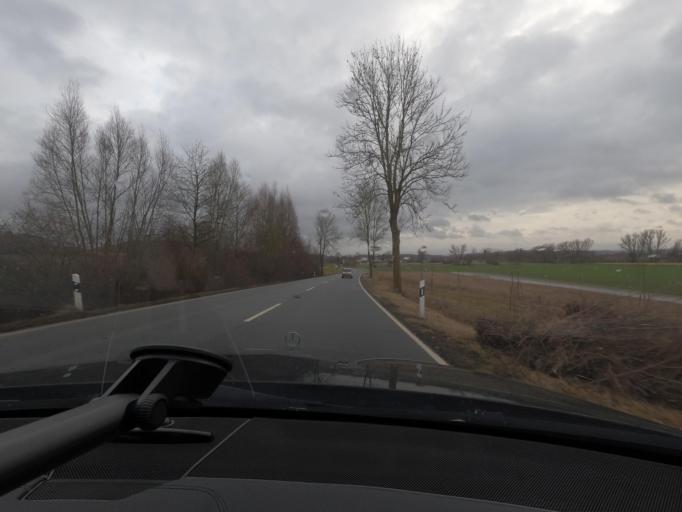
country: DE
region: Hesse
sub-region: Regierungsbezirk Kassel
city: Volkmarsen
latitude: 51.4246
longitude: 9.1237
